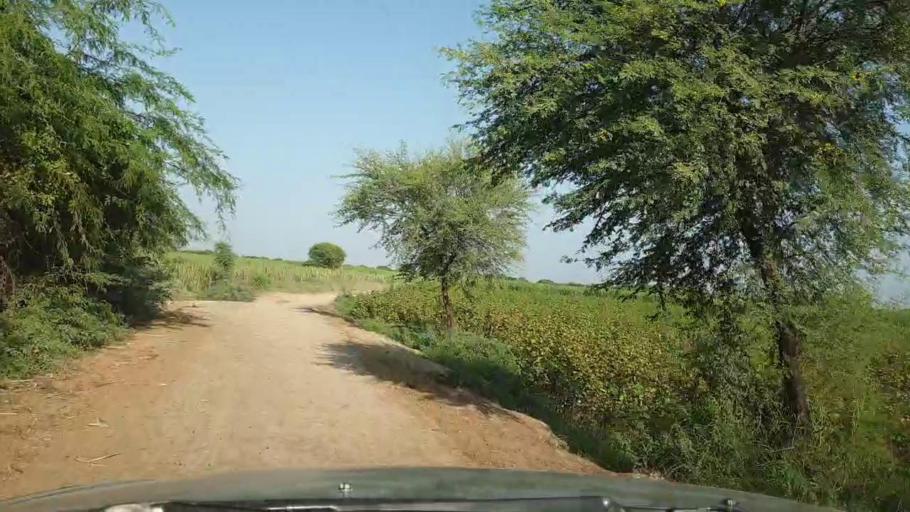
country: PK
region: Sindh
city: Tando Ghulam Ali
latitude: 25.0978
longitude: 68.8788
